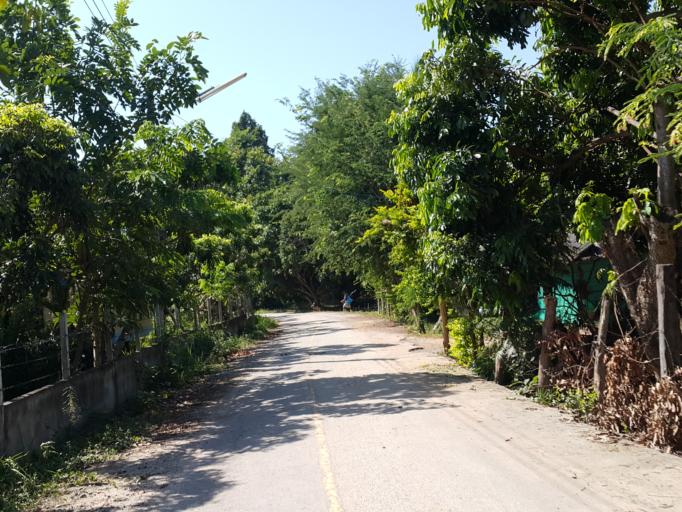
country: TH
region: Chiang Mai
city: San Sai
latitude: 18.8746
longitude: 99.1619
